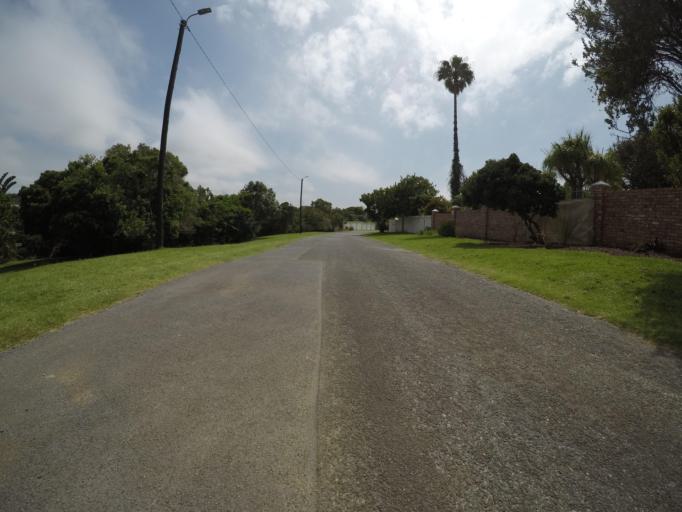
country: ZA
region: Eastern Cape
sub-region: Buffalo City Metropolitan Municipality
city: East London
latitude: -32.9369
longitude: 28.0238
